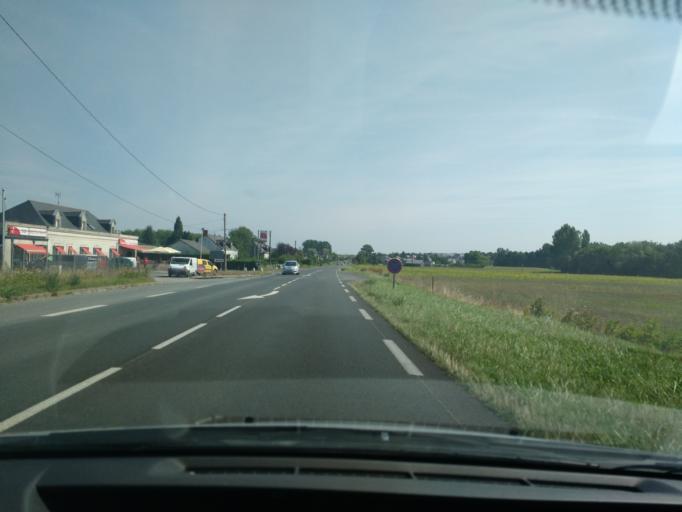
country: FR
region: Pays de la Loire
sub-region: Departement de Maine-et-Loire
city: Corne
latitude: 47.4719
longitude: -0.3672
